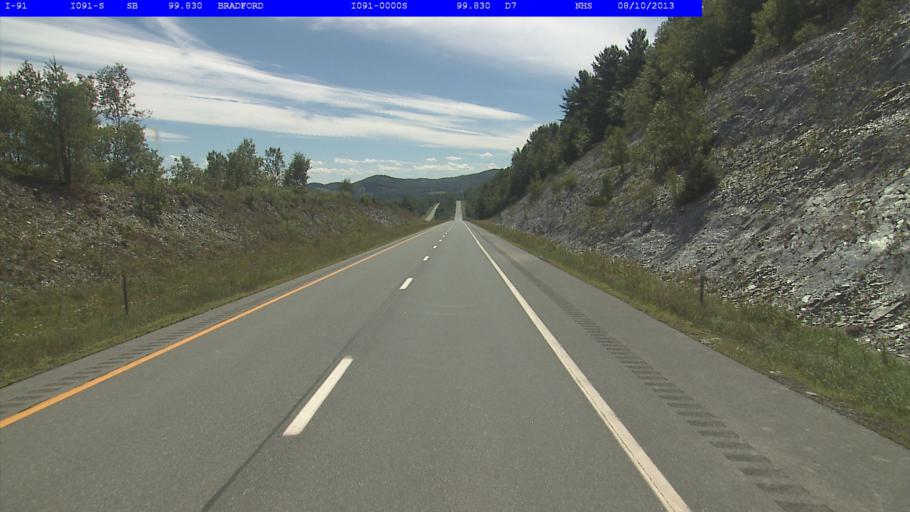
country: US
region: New Hampshire
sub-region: Grafton County
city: Haverhill
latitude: 44.0132
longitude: -72.1230
